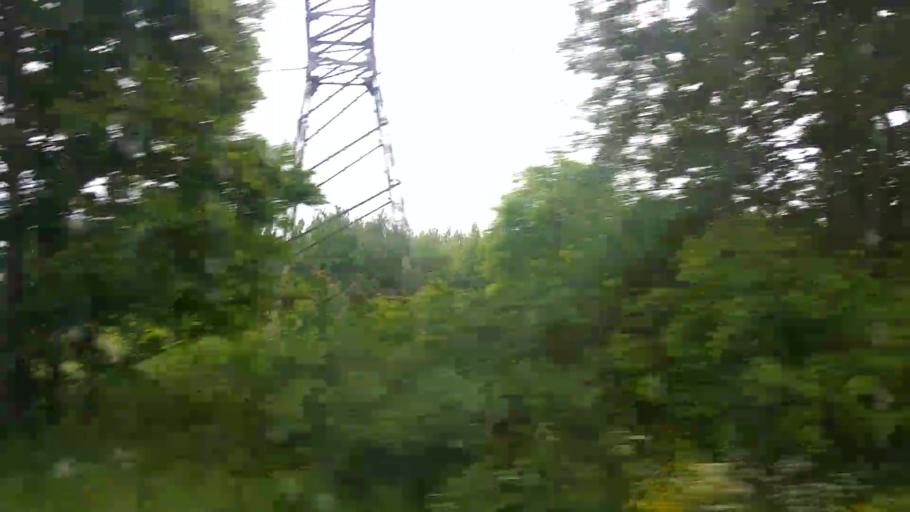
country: RU
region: Moskovskaya
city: Ozherel'ye
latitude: 54.8450
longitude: 38.2682
